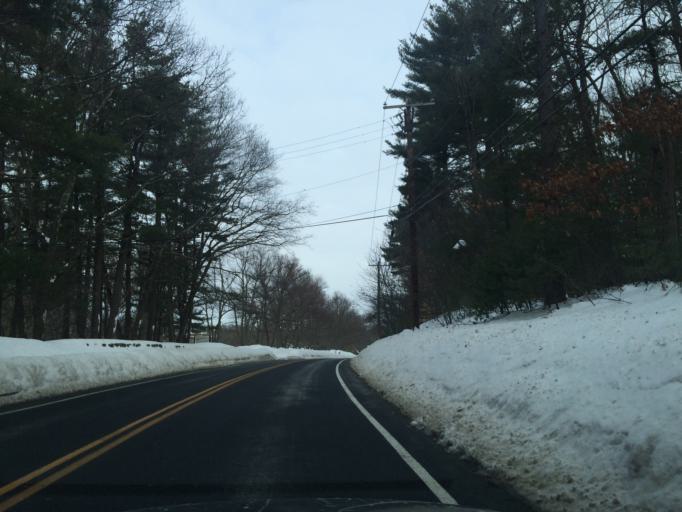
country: US
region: Massachusetts
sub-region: Middlesex County
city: Weston
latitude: 42.3480
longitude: -71.3063
